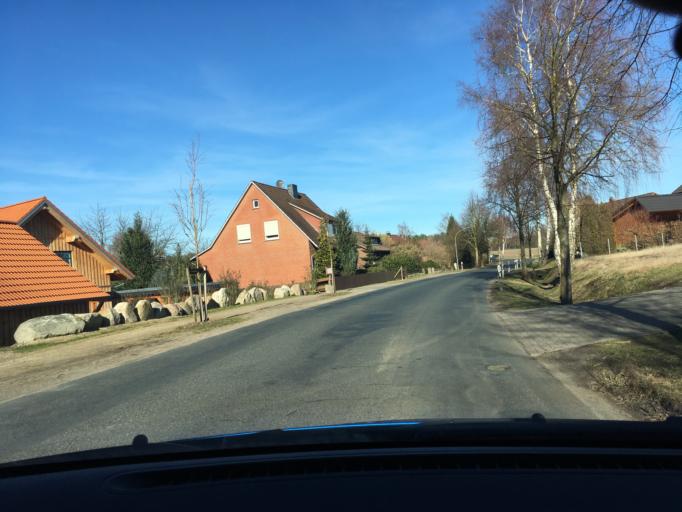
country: DE
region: Lower Saxony
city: Schwienau
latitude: 52.9811
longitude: 10.4446
